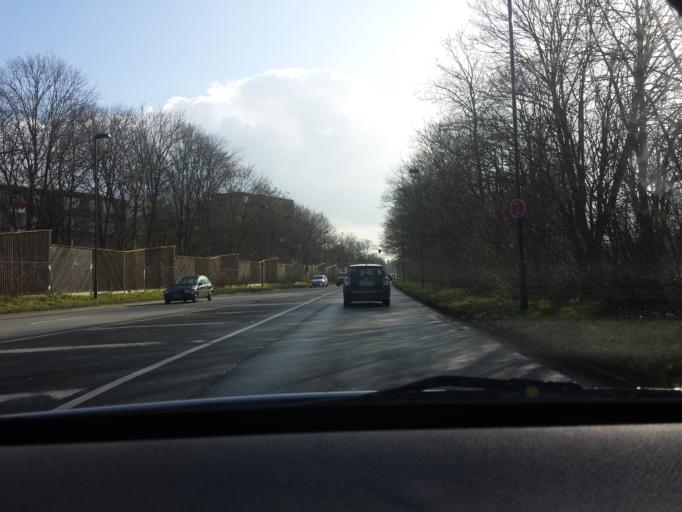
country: DE
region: North Rhine-Westphalia
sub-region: Regierungsbezirk Dusseldorf
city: Hilden
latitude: 51.1399
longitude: 6.9042
